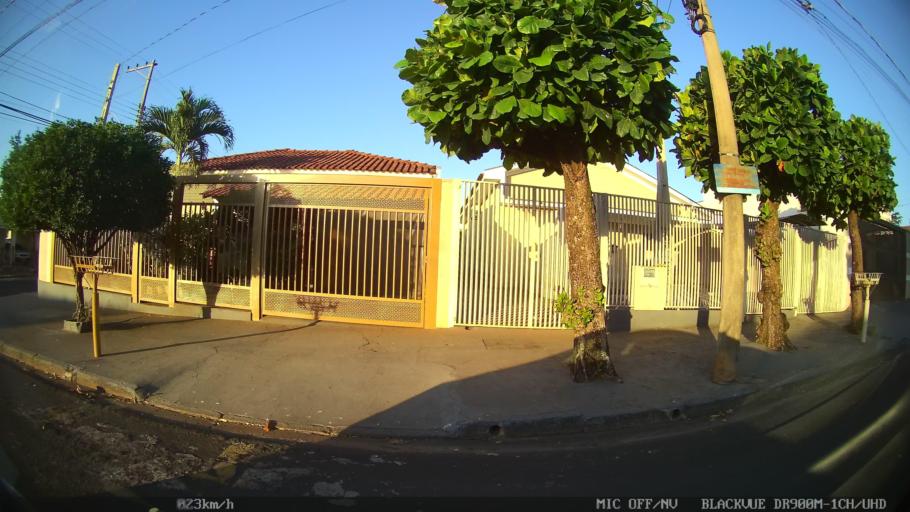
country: BR
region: Sao Paulo
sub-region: Sao Jose Do Rio Preto
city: Sao Jose do Rio Preto
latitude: -20.7889
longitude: -49.3710
